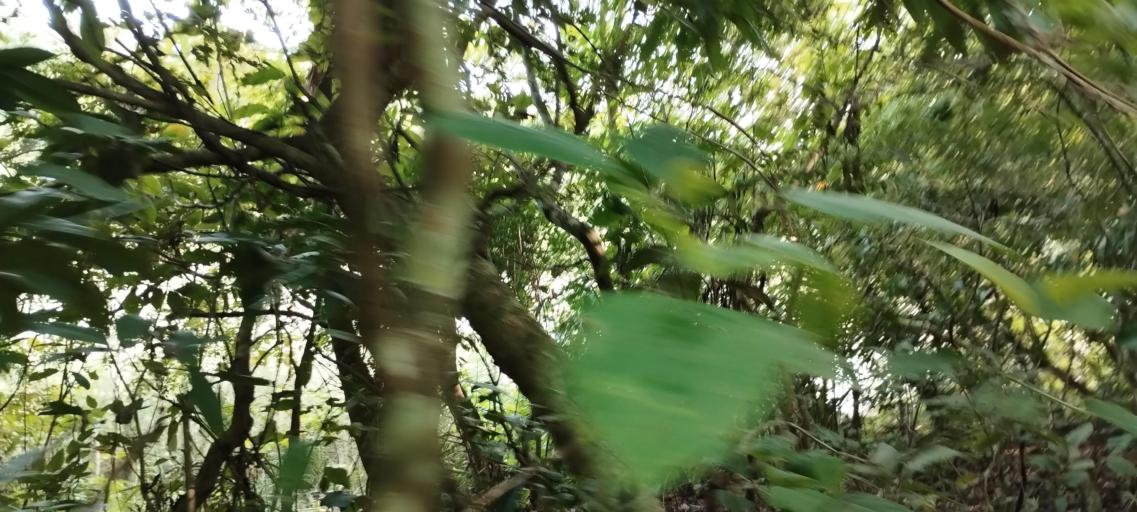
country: NP
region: Far Western
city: Tikapur
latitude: 28.4670
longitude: 81.2481
